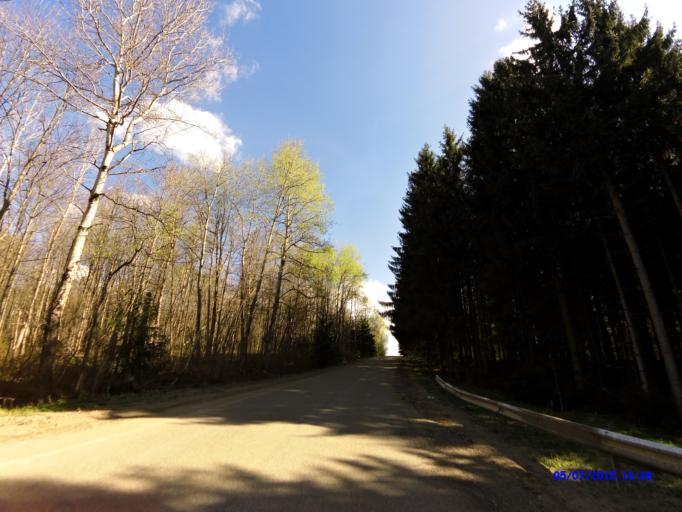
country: US
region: New York
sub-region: Cattaraugus County
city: Little Valley
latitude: 42.3125
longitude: -78.6814
